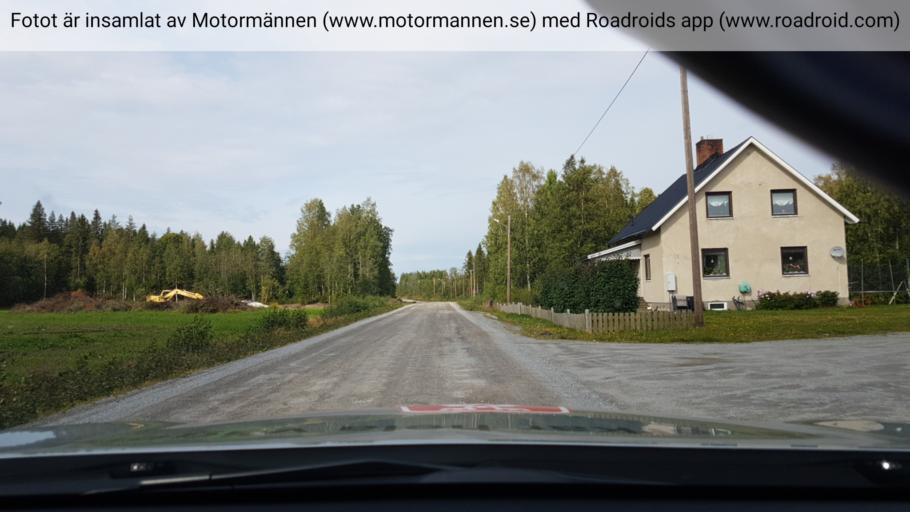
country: SE
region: Vaesterbotten
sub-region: Bjurholms Kommun
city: Bjurholm
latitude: 63.8700
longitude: 19.4578
